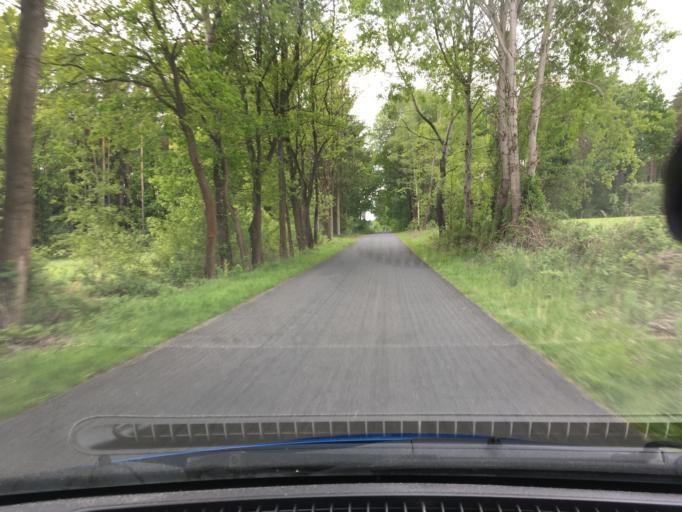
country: DE
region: Lower Saxony
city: Rehlingen
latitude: 53.1019
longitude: 10.2491
